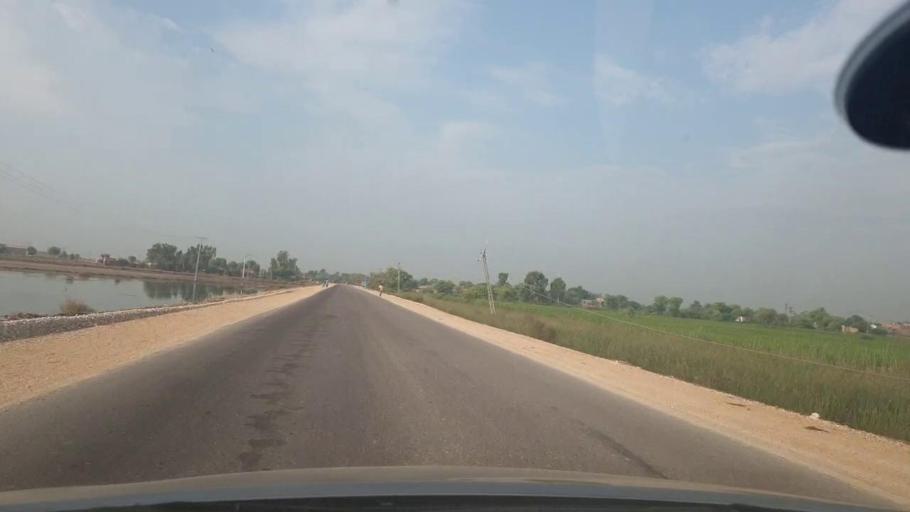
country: PK
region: Sindh
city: Jacobabad
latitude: 28.2188
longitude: 68.3716
